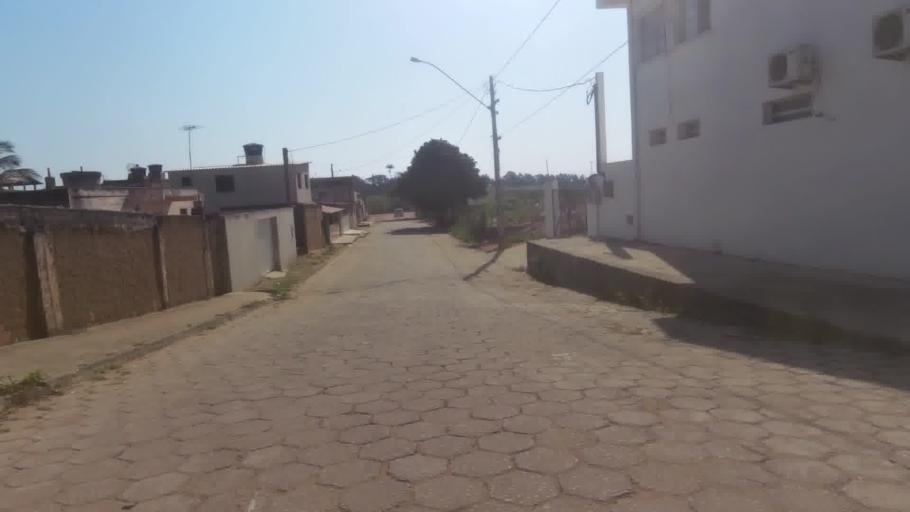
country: BR
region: Espirito Santo
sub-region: Itapemirim
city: Itapemirim
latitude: -21.0148
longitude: -40.8152
